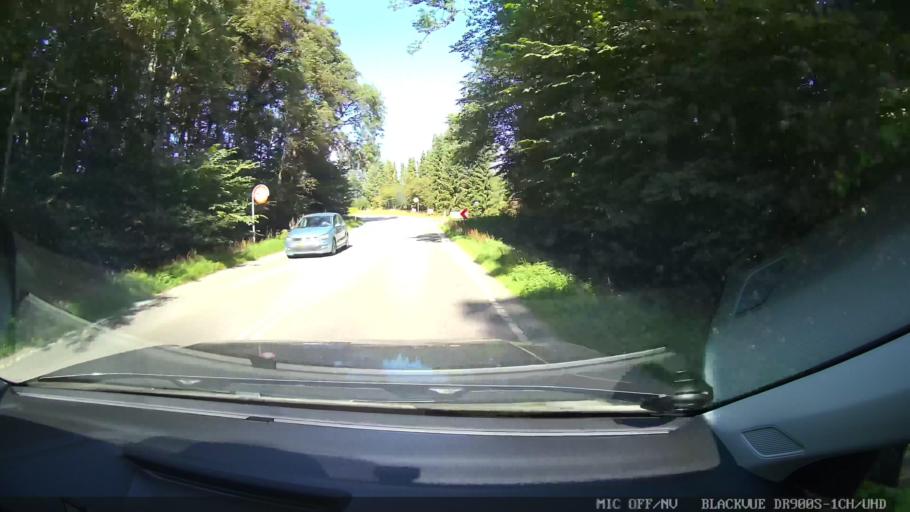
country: DK
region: North Denmark
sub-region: Mariagerfjord Kommune
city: Mariager
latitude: 56.6083
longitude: 9.9949
